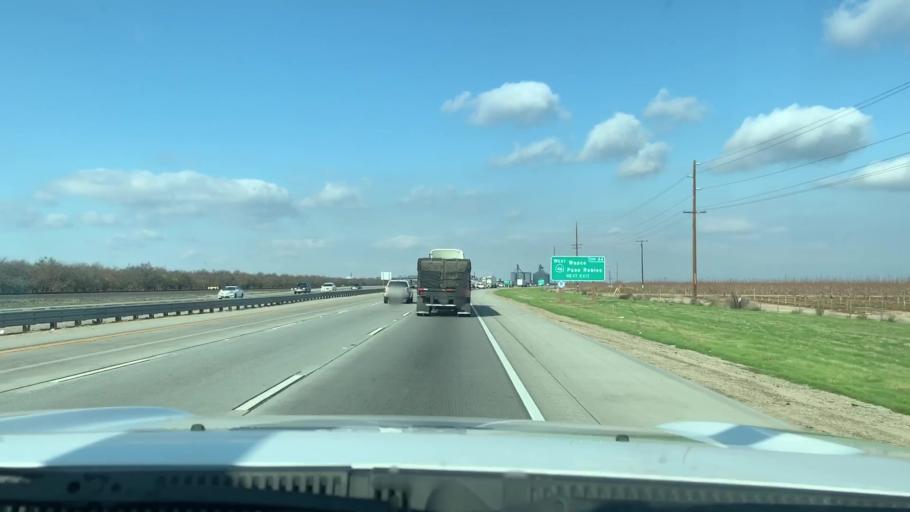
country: US
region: California
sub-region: Kern County
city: McFarland
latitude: 35.5824
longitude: -119.2036
